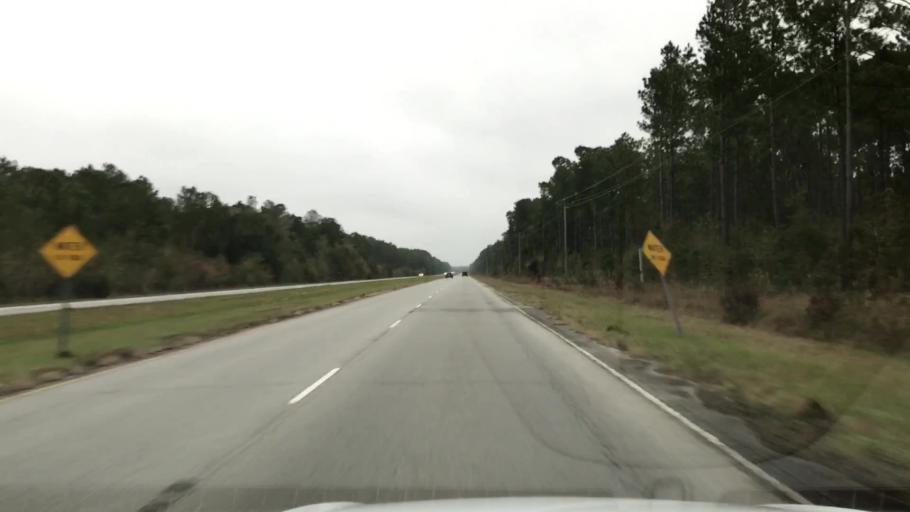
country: US
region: South Carolina
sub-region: Charleston County
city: Awendaw
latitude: 33.0075
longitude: -79.6402
